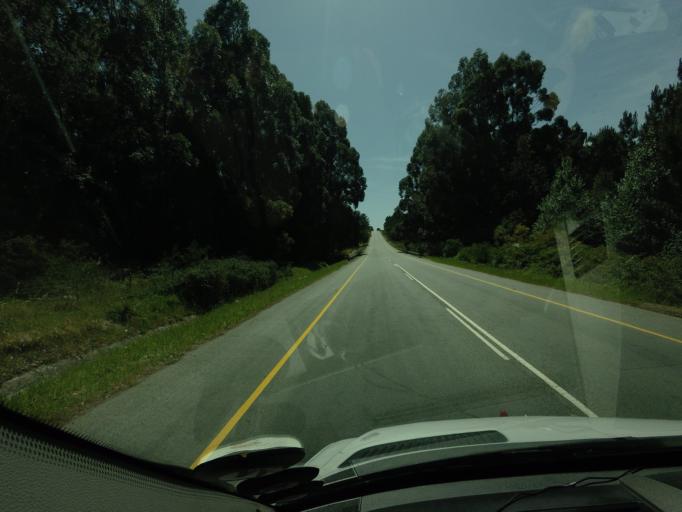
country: ZA
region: Western Cape
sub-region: Overberg District Municipality
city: Hermanus
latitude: -34.3039
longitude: 19.1353
